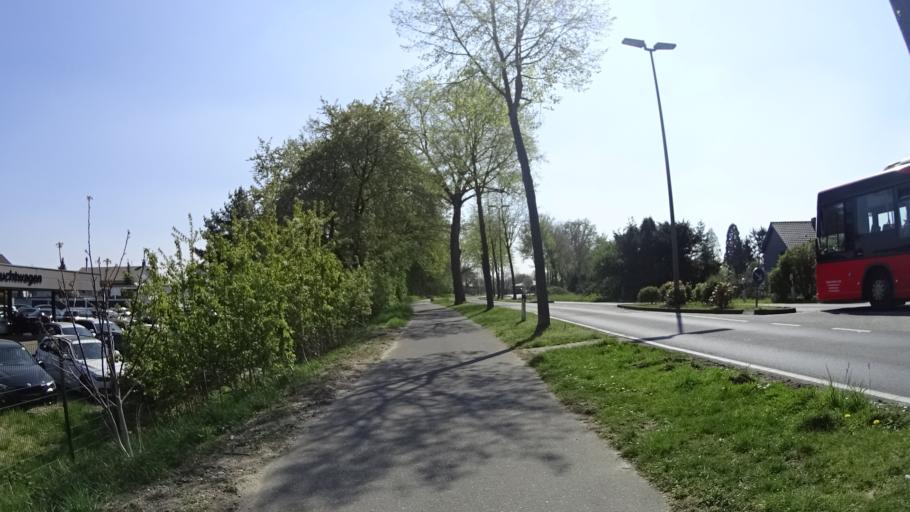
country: DE
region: North Rhine-Westphalia
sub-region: Regierungsbezirk Dusseldorf
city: Meerbusch
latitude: 51.3144
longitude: 6.6794
